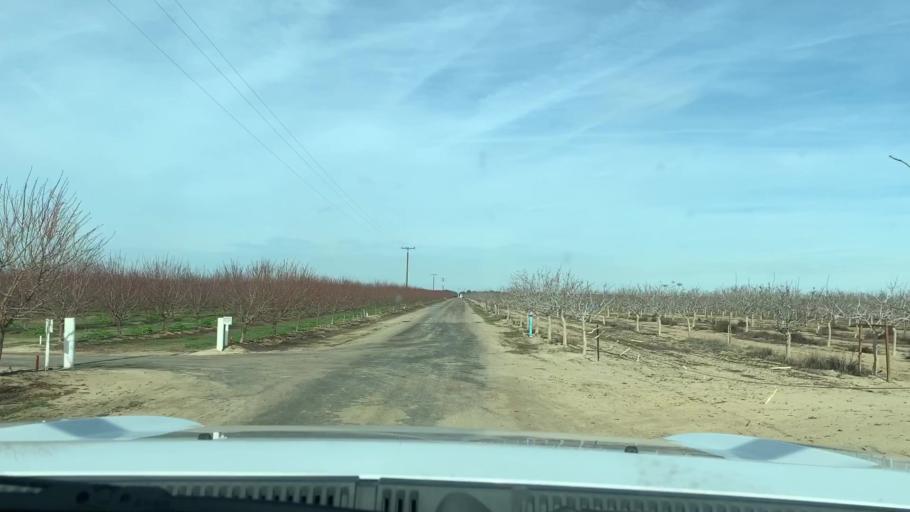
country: US
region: California
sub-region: Kern County
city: Lost Hills
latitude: 35.6083
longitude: -119.5357
